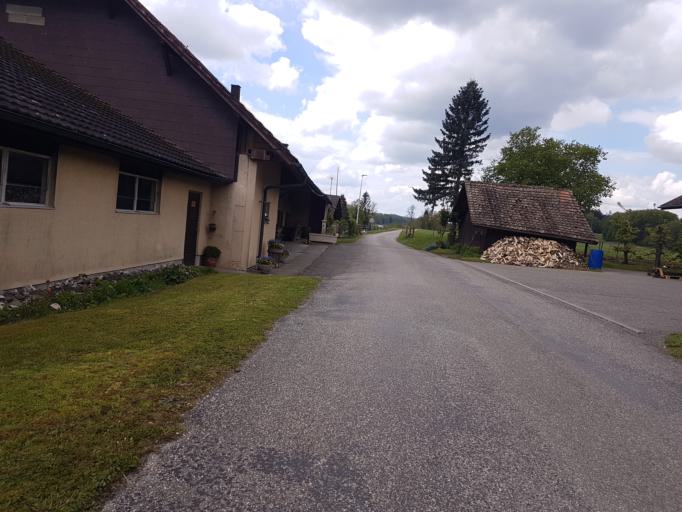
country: CH
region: Solothurn
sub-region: Bezirk Gaeu
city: Wolfwil
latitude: 47.2627
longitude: 7.7935
